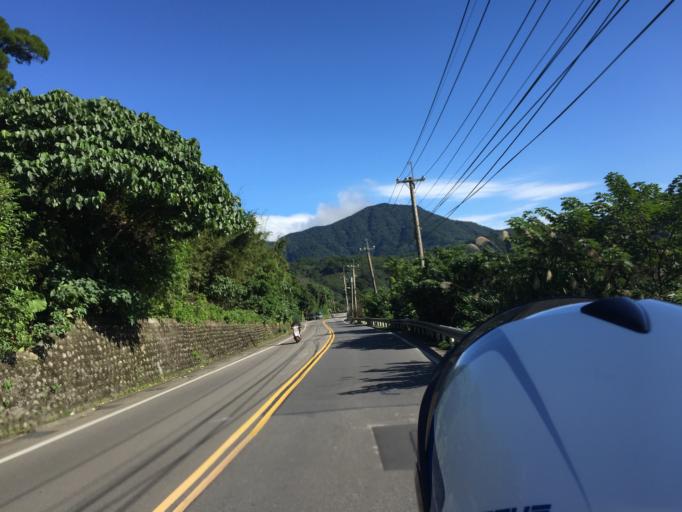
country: TW
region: Taipei
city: Taipei
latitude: 25.1824
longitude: 121.4610
